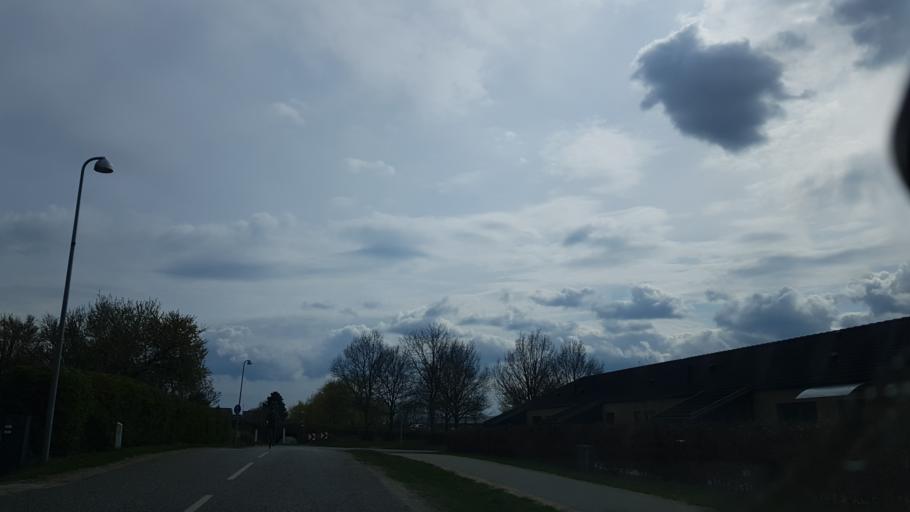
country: DK
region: Capital Region
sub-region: Allerod Kommune
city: Lillerod
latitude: 55.8812
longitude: 12.3460
